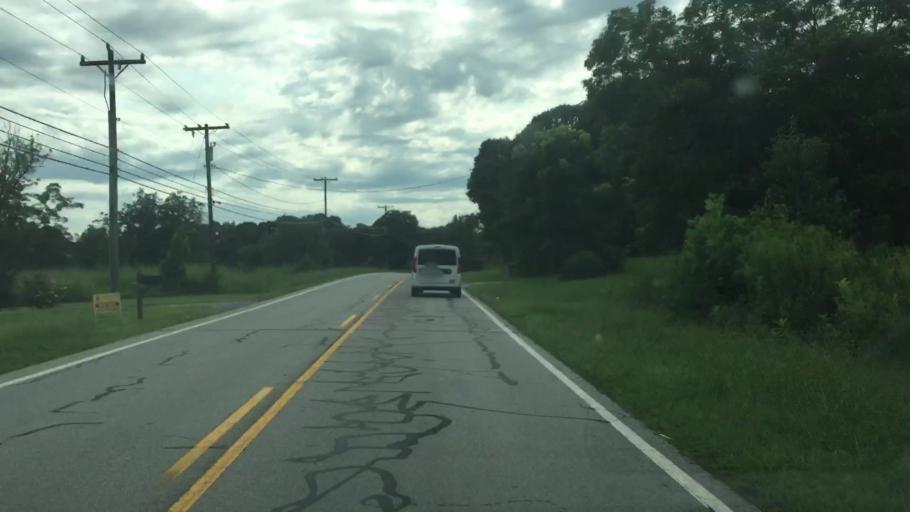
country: US
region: North Carolina
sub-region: Rowan County
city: Franklin
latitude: 35.6595
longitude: -80.5628
